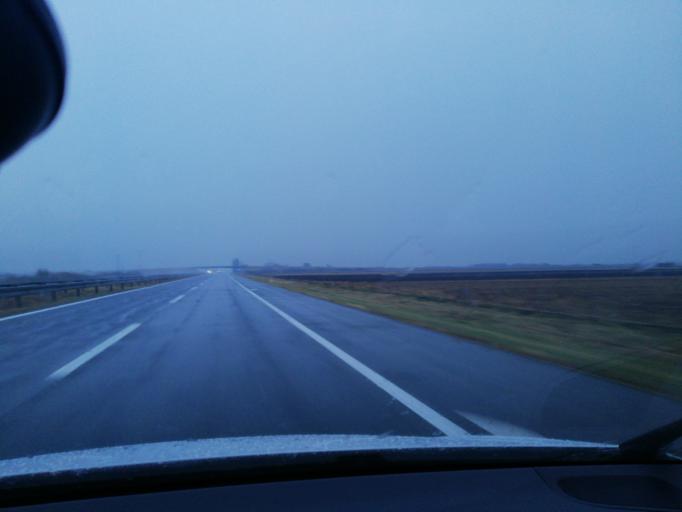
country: RS
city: Sasinci
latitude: 44.9731
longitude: 19.7572
